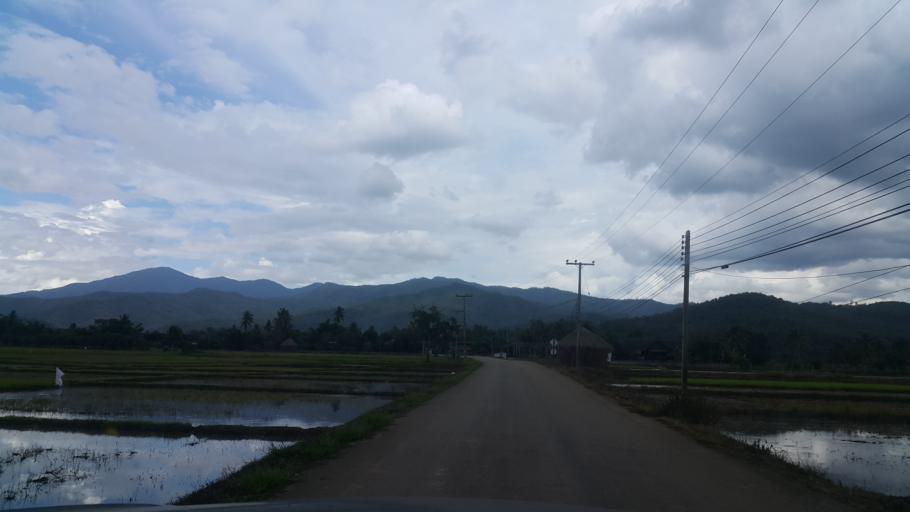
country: TH
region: Chiang Mai
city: Mae Taeng
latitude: 19.1874
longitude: 98.9987
